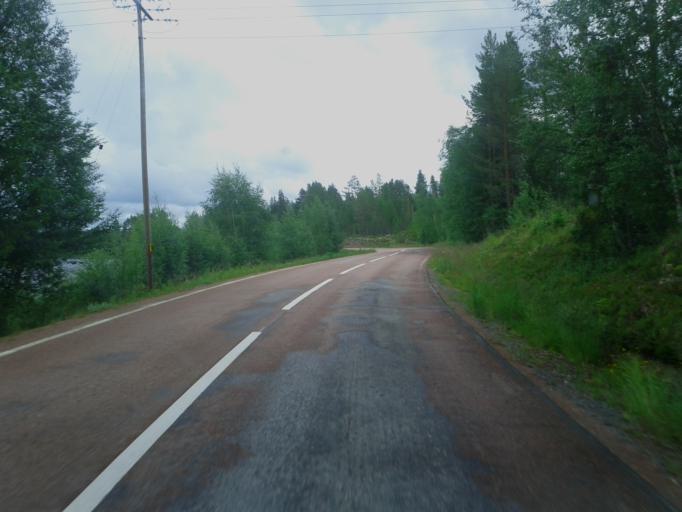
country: NO
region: Hedmark
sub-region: Trysil
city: Innbygda
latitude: 61.8512
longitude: 12.6990
